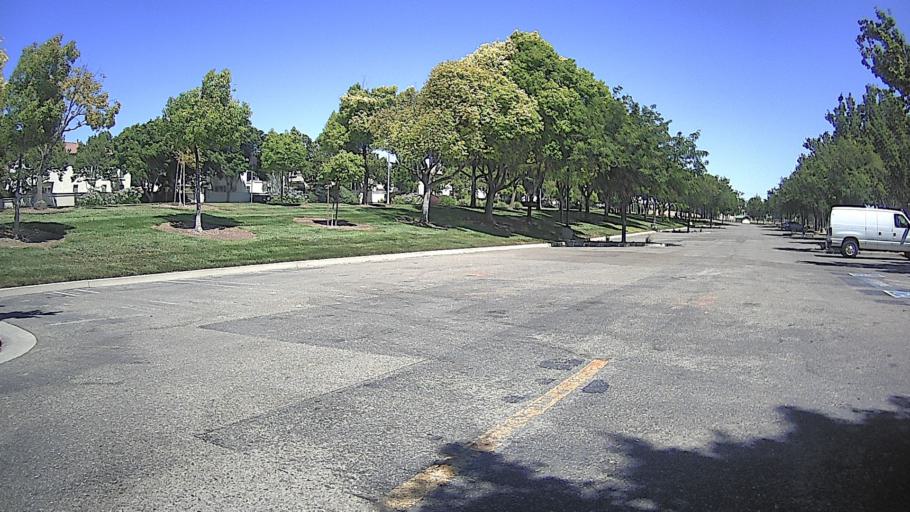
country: US
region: California
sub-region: Alameda County
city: Pleasanton
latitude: 37.7123
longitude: -121.8753
